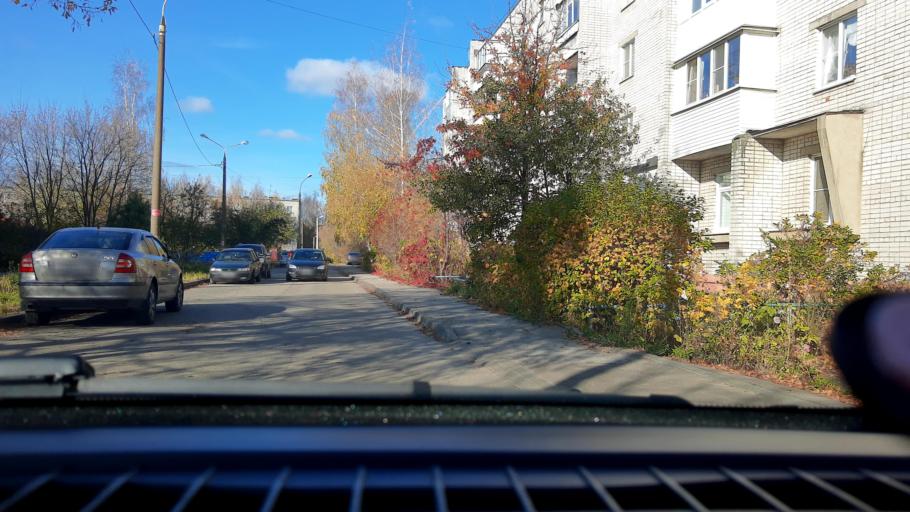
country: RU
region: Nizjnij Novgorod
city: Kstovo
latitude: 56.1496
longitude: 44.2194
